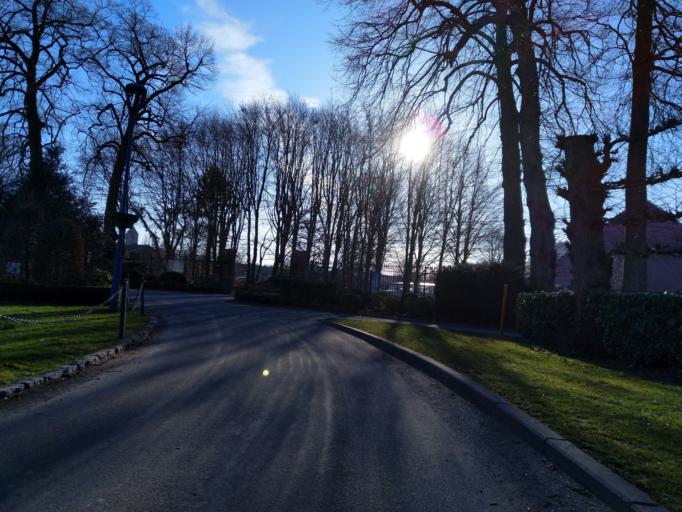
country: BE
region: Wallonia
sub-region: Province du Hainaut
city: Jurbise
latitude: 50.5338
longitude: 3.9069
